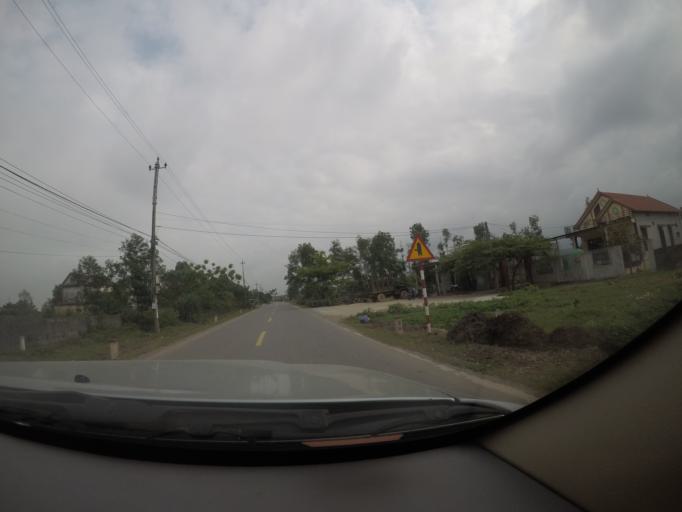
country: VN
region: Quang Binh
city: Kwang Binh
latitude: 17.4325
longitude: 106.5826
